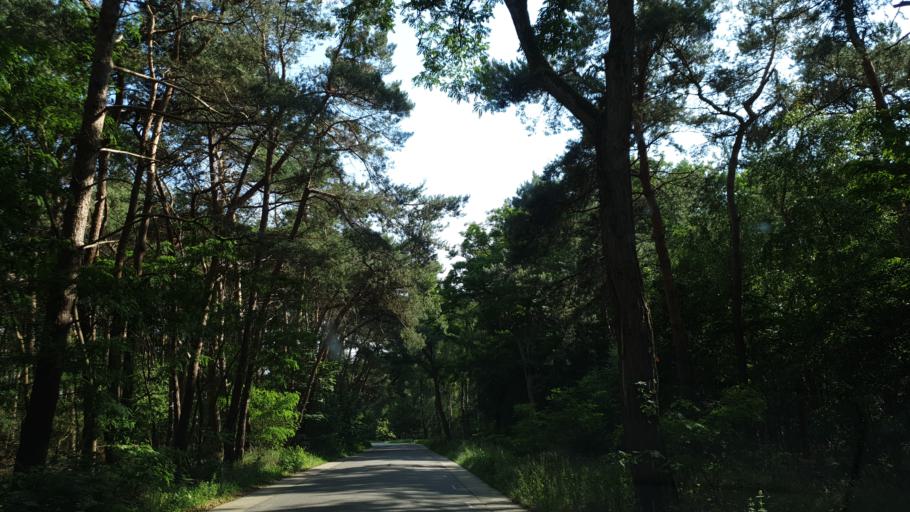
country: NL
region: Limburg
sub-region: Gemeente Weert
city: Weert
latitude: 51.2634
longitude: 5.6444
